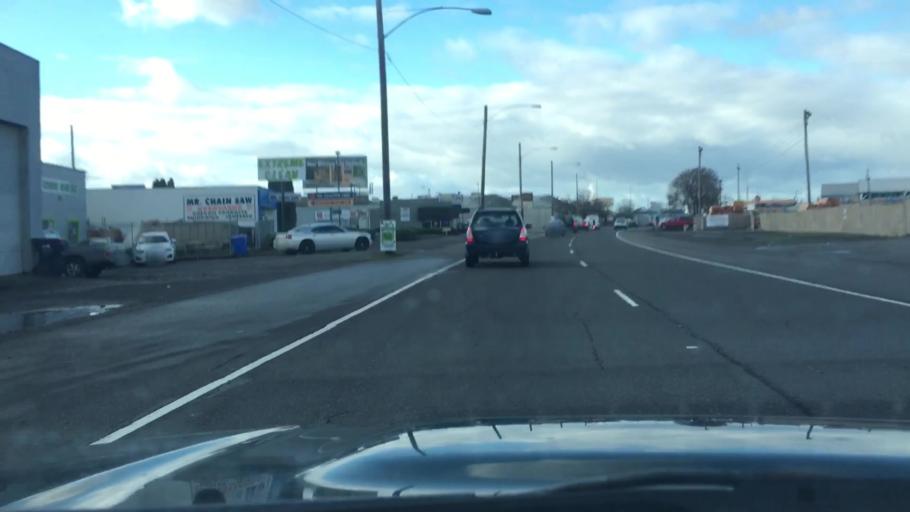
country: US
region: Oregon
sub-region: Lane County
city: Eugene
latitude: 44.0534
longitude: -123.1230
